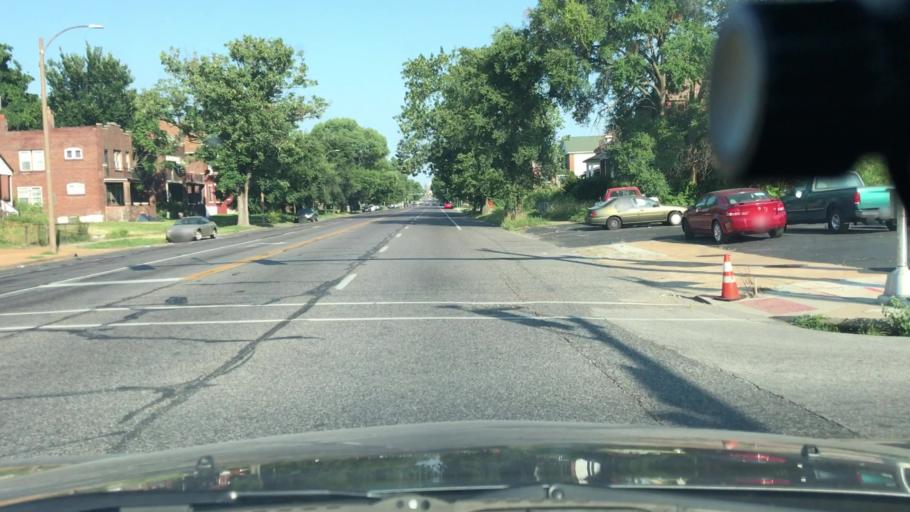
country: US
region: Missouri
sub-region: City of Saint Louis
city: St. Louis
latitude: 38.6508
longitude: -90.2386
